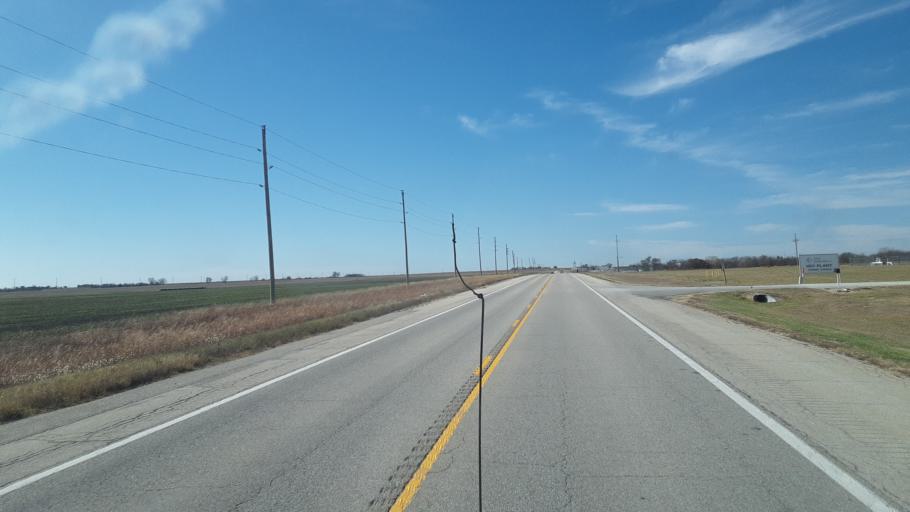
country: US
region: Kansas
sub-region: McPherson County
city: Inman
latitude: 38.3770
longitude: -97.8384
